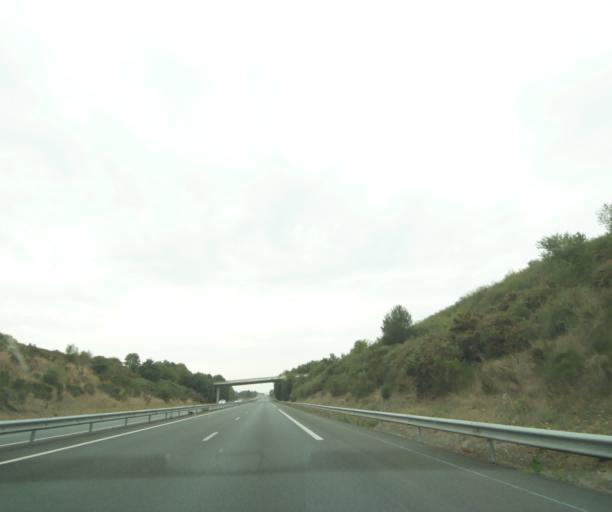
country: FR
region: Pays de la Loire
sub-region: Departement de la Vendee
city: Saint-Martin-des-Noyers
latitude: 46.7118
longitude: -1.1569
